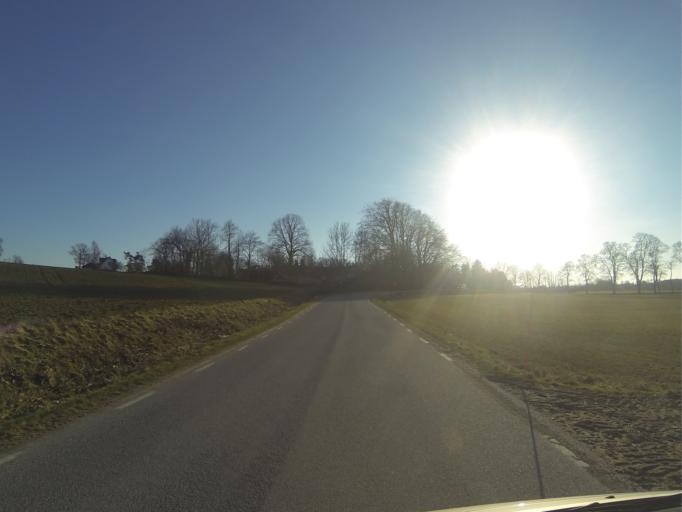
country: SE
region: Skane
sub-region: Horby Kommun
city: Hoerby
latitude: 55.8398
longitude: 13.6268
